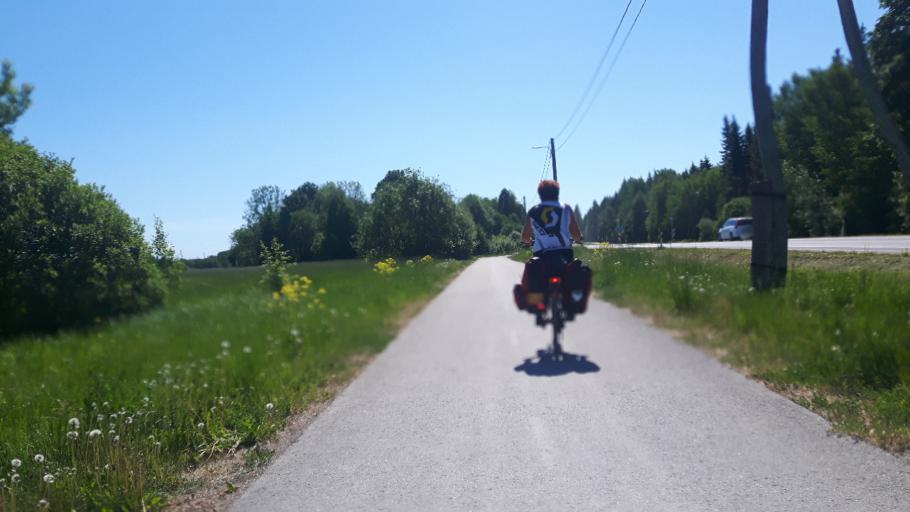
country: EE
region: Harju
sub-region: Saku vald
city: Saku
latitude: 59.2875
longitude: 24.6622
